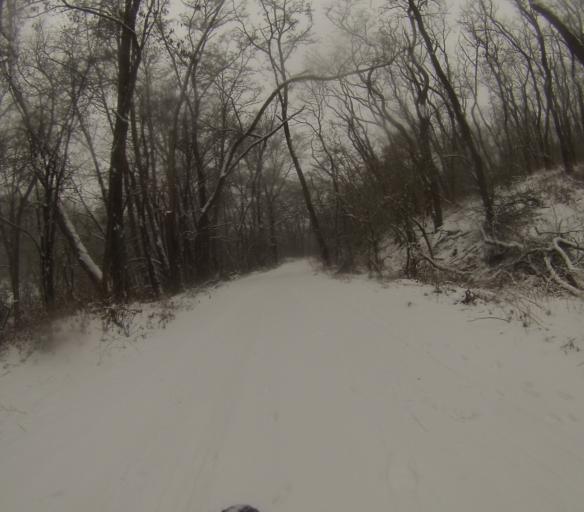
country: CZ
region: South Moravian
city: Orechov
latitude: 49.1324
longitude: 16.5355
